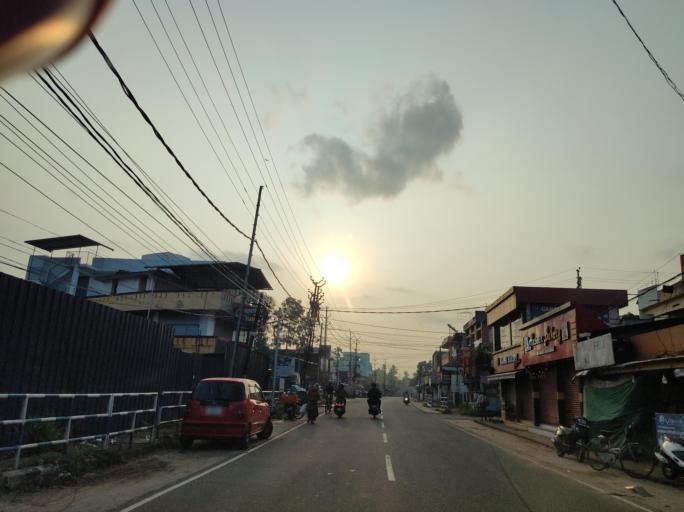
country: IN
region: Kerala
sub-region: Alappuzha
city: Kayankulam
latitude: 9.1755
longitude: 76.5067
